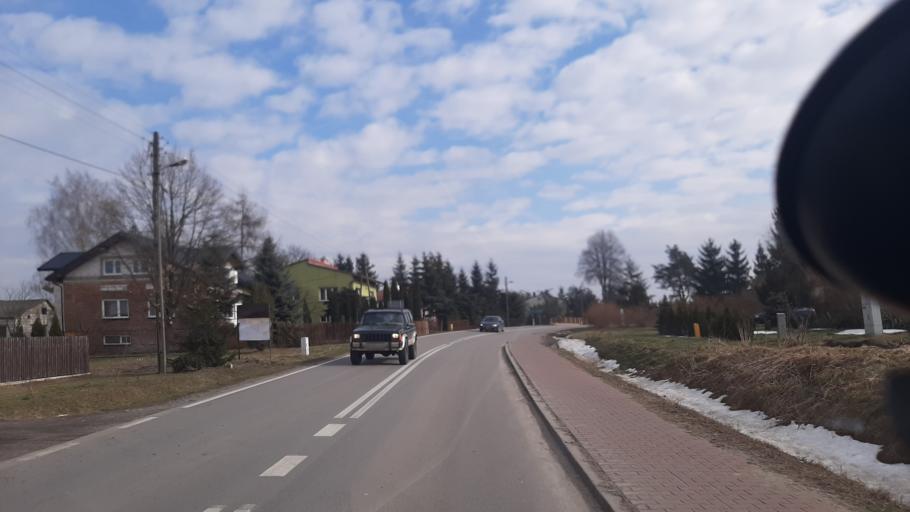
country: PL
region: Lublin Voivodeship
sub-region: Powiat lubelski
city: Niemce
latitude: 51.3618
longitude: 22.5942
